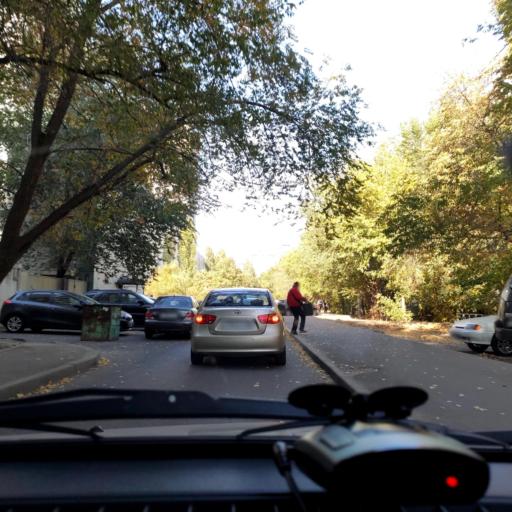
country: RU
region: Voronezj
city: Voronezh
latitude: 51.6419
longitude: 39.2325
